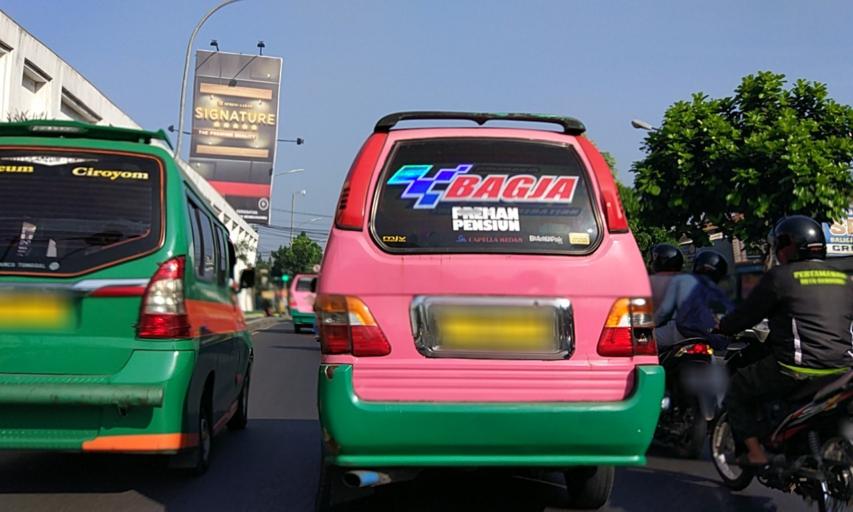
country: ID
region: West Java
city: Bandung
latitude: -6.9020
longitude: 107.6542
